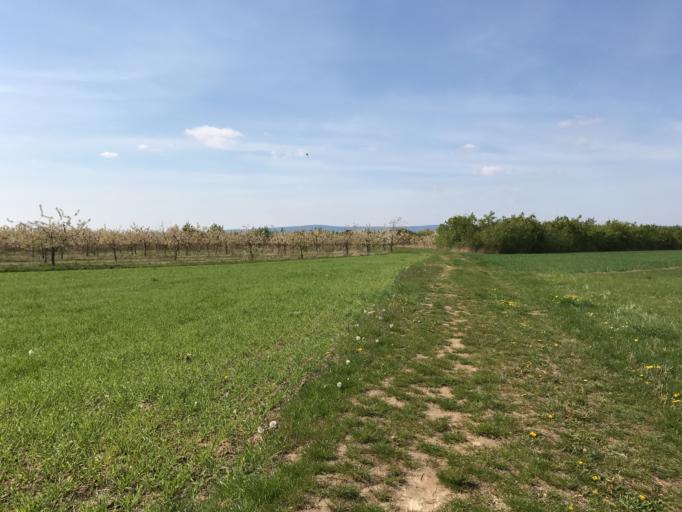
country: DE
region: Rheinland-Pfalz
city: Budenheim
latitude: 49.9906
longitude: 8.1514
